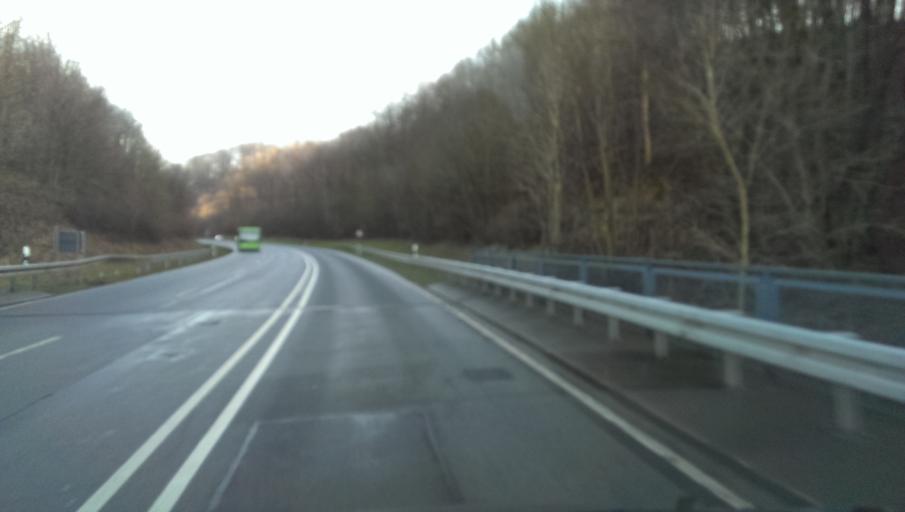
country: DE
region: North Rhine-Westphalia
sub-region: Regierungsbezirk Detmold
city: Bad Driburg
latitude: 51.7327
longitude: 8.9980
